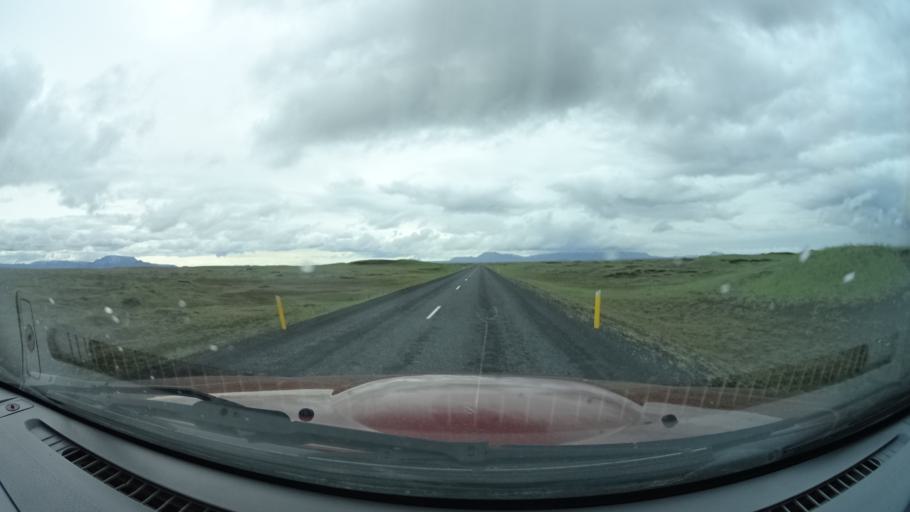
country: IS
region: Northeast
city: Laugar
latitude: 65.6397
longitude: -16.3118
